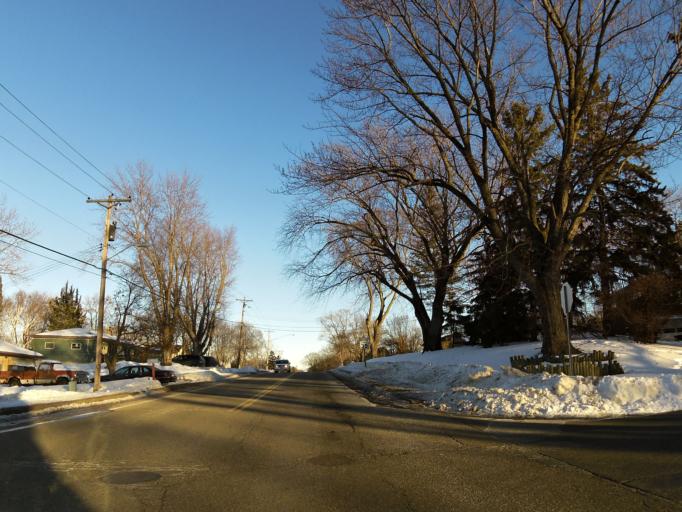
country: US
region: Minnesota
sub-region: Ramsey County
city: North Saint Paul
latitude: 45.0208
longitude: -93.0268
